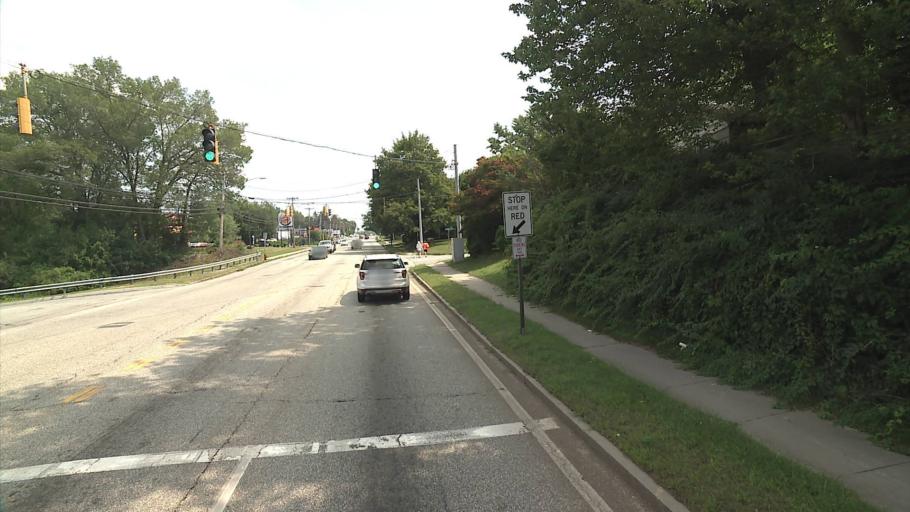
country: US
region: Connecticut
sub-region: New London County
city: Norwich
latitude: 41.5133
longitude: -72.1078
